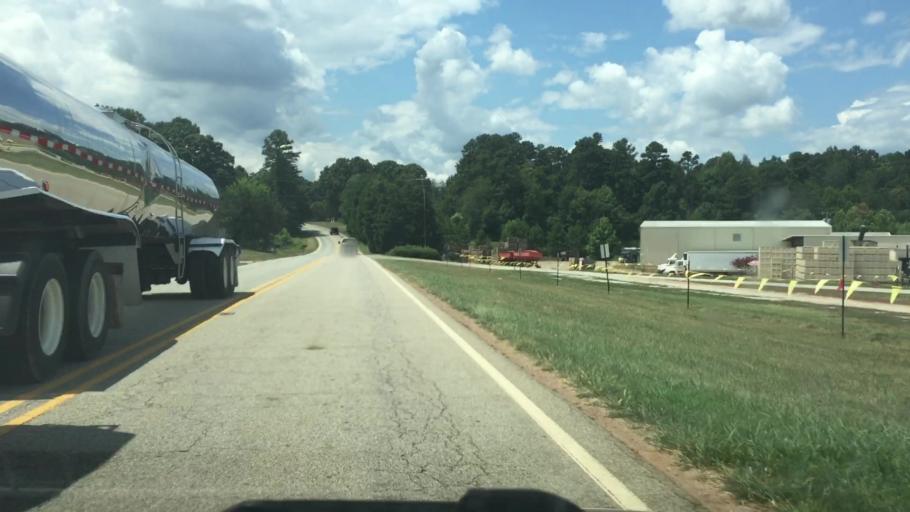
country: US
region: North Carolina
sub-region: Rowan County
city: Landis
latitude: 35.6163
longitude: -80.6523
